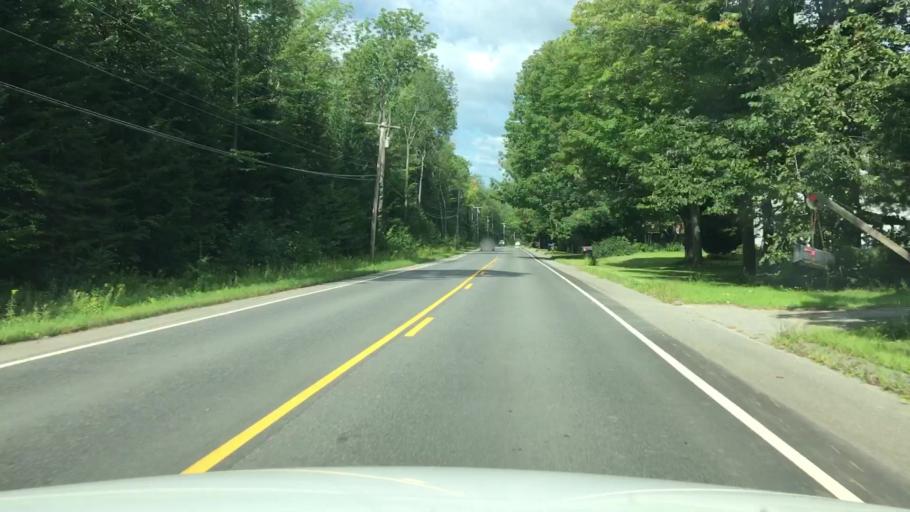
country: US
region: Maine
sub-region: Somerset County
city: Skowhegan
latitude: 44.7476
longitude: -69.6991
